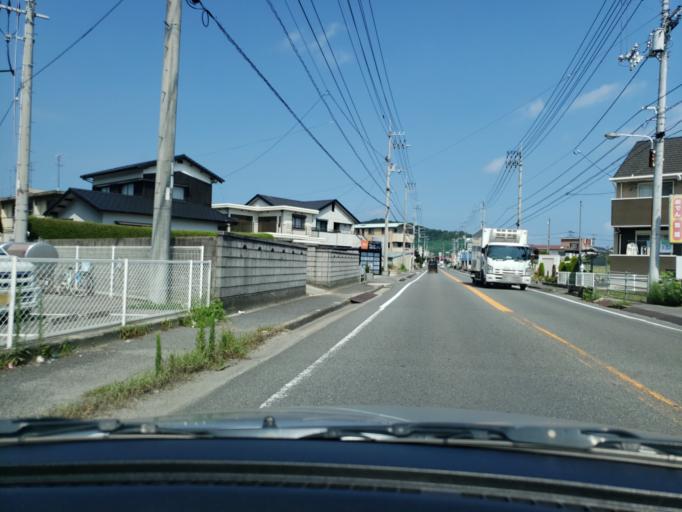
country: JP
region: Ehime
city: Hojo
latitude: 34.0988
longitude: 132.9712
